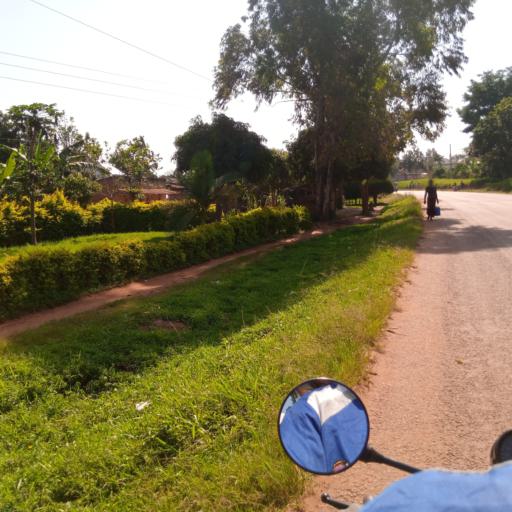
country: UG
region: Central Region
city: Masaka
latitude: -0.3777
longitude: 31.7119
